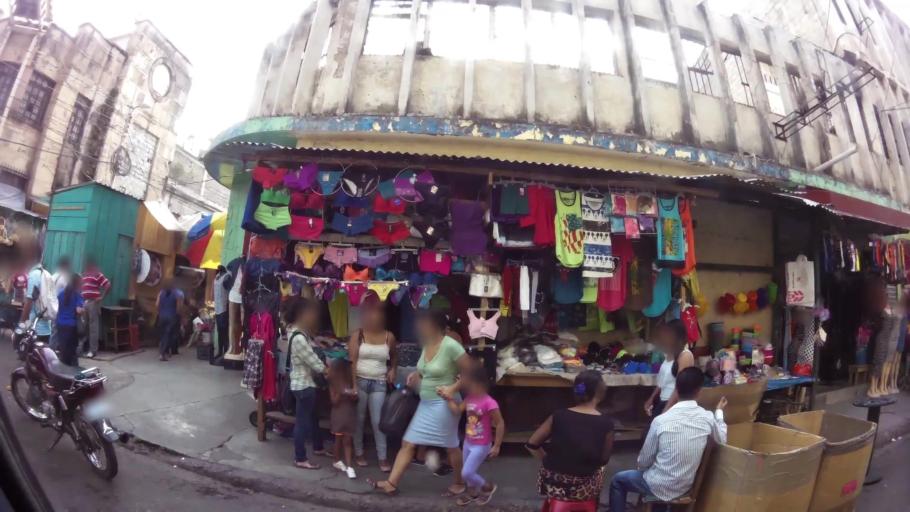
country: HN
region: Francisco Morazan
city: Tegucigalpa
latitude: 14.1021
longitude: -87.2078
